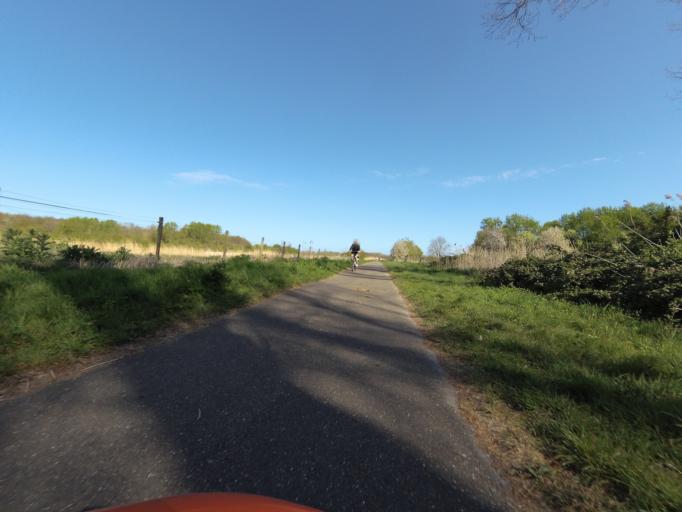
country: NL
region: Flevoland
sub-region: Gemeente Almere
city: Almere Stad
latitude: 52.3693
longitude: 5.1639
